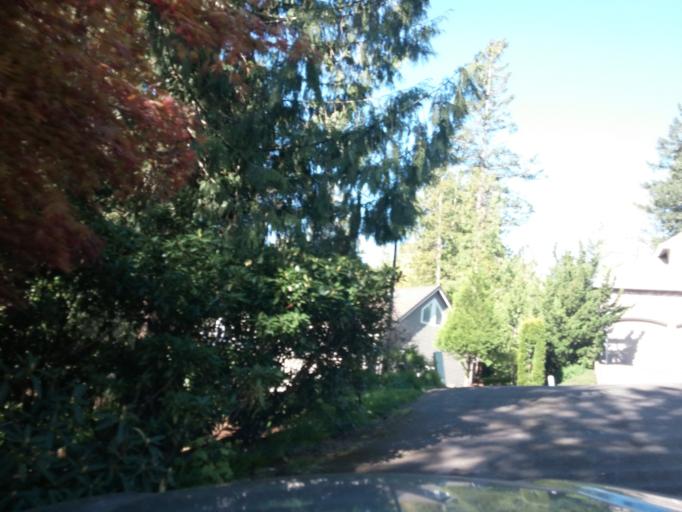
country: US
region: Oregon
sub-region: Washington County
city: West Haven
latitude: 45.5363
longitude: -122.7851
